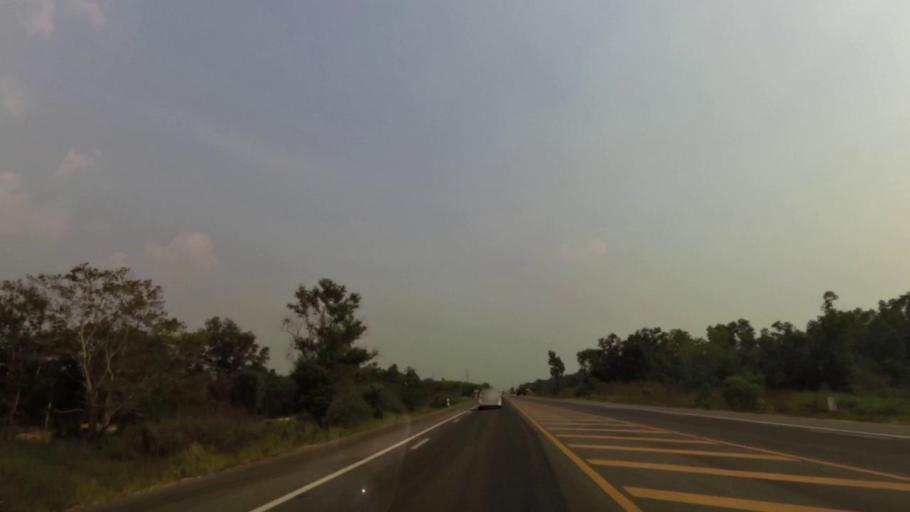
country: TH
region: Rayong
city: Klaeng
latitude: 12.8072
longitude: 101.6499
